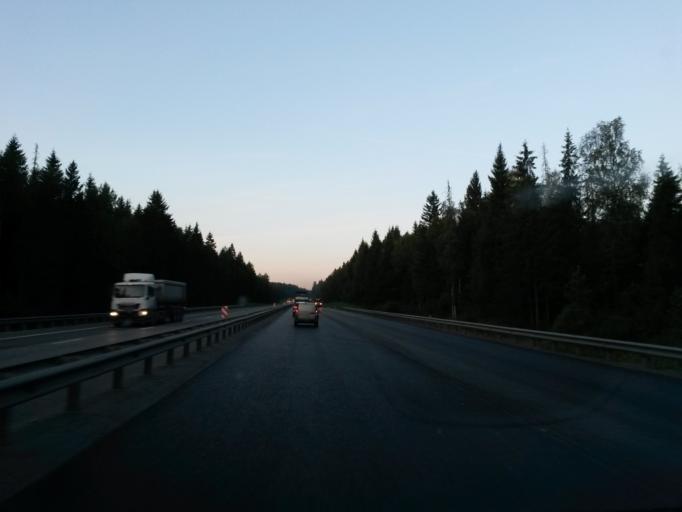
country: RU
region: Moskovskaya
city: Svatkovo
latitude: 56.3131
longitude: 38.2448
